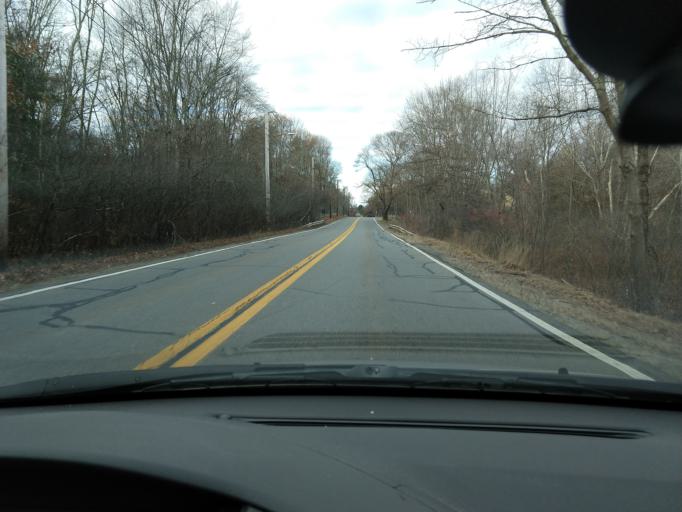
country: US
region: Massachusetts
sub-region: Middlesex County
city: Lincoln
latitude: 42.4488
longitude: -71.2735
